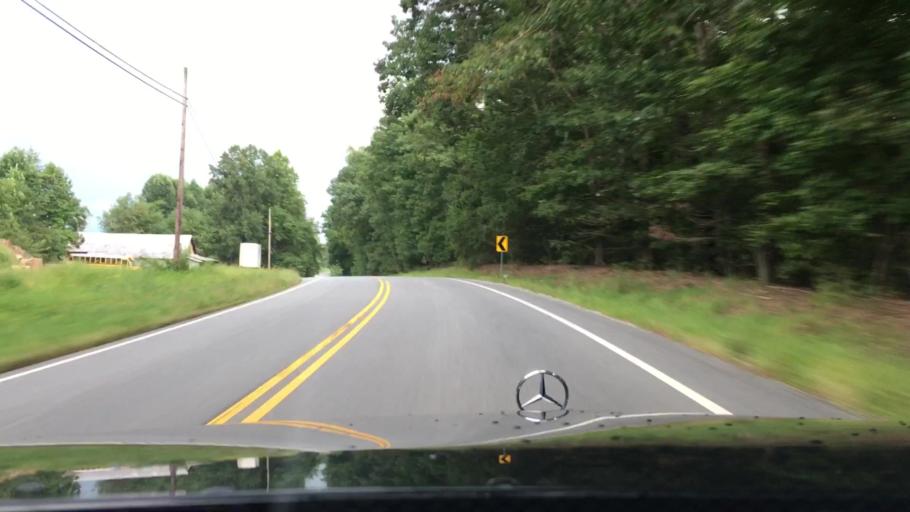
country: US
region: Virginia
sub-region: Nelson County
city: Lovingston
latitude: 37.7934
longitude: -78.9740
